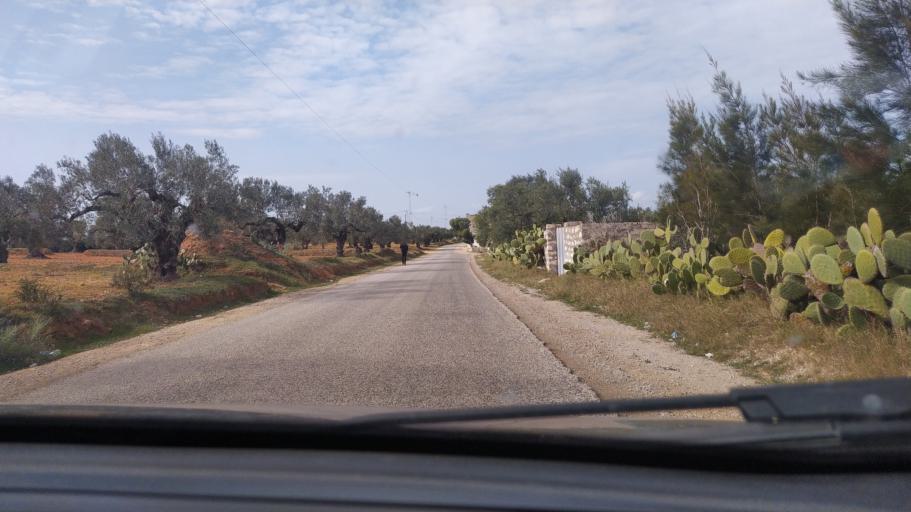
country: TN
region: Al Munastir
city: Sidi Bin Nur
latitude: 35.5299
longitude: 10.9631
